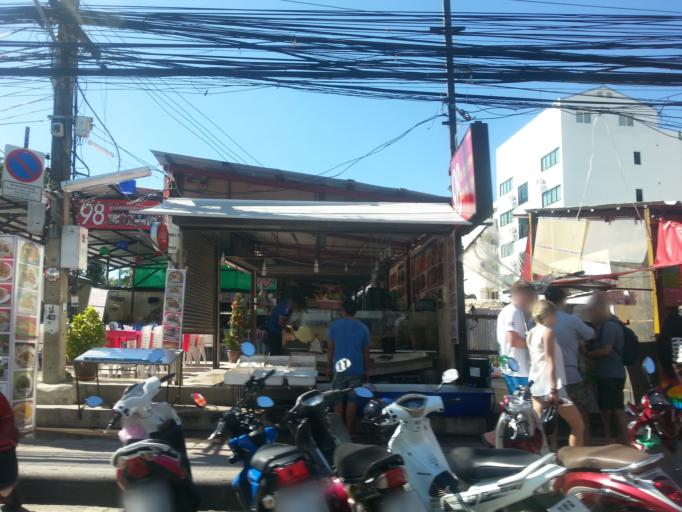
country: TH
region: Phuket
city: Patong
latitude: 7.8957
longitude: 98.2991
